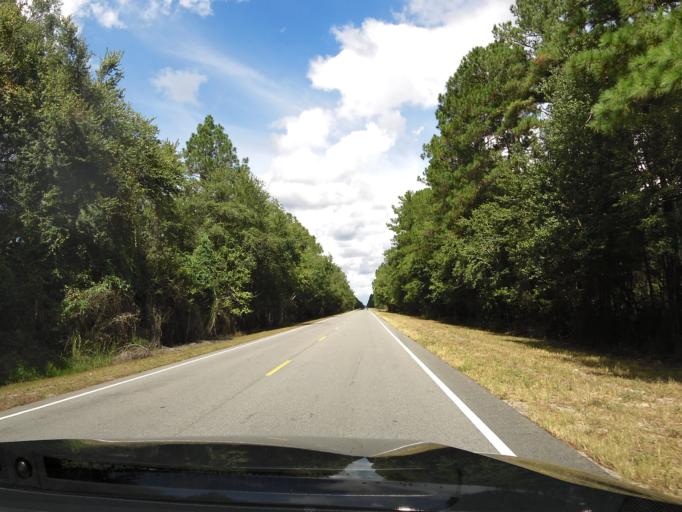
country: US
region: Georgia
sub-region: Charlton County
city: Folkston
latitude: 30.9425
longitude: -82.0225
